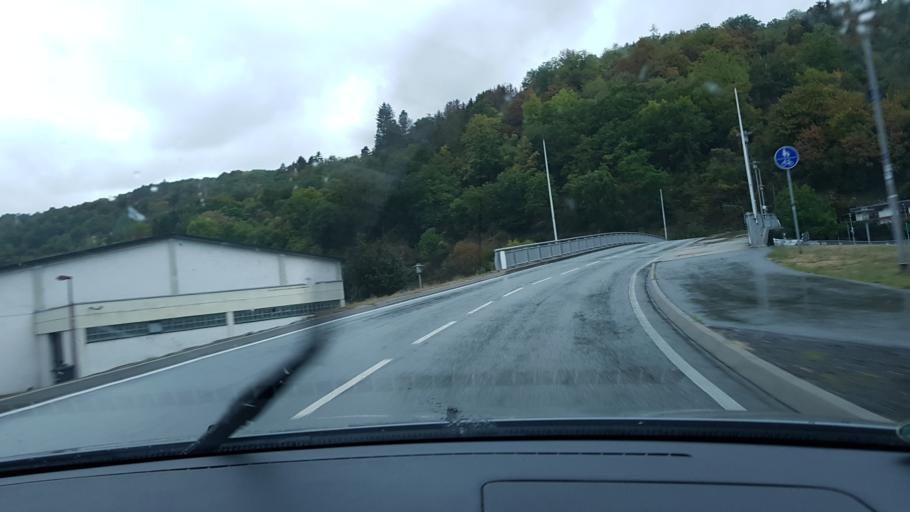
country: DE
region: Rheinland-Pfalz
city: Dausenau
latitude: 50.3280
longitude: 7.7587
